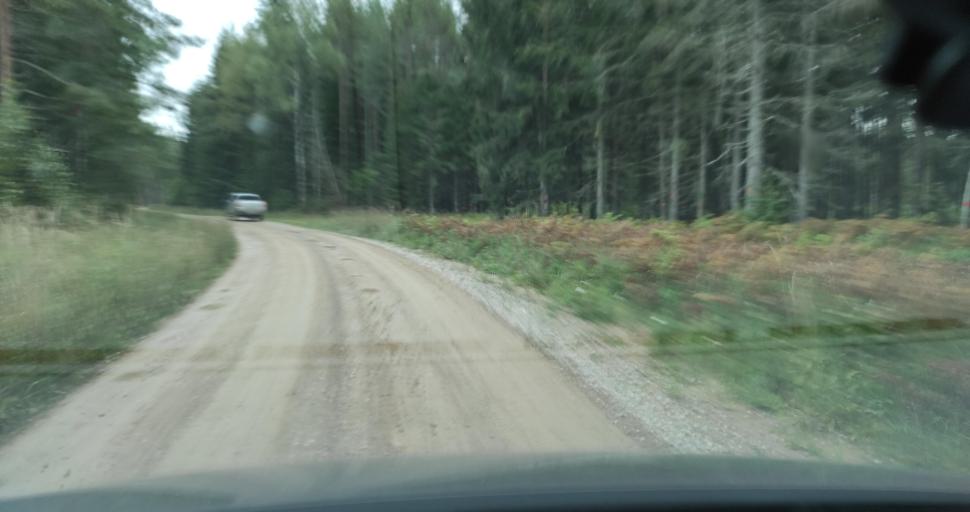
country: LV
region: Talsu Rajons
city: Stende
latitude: 57.0289
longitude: 22.3335
